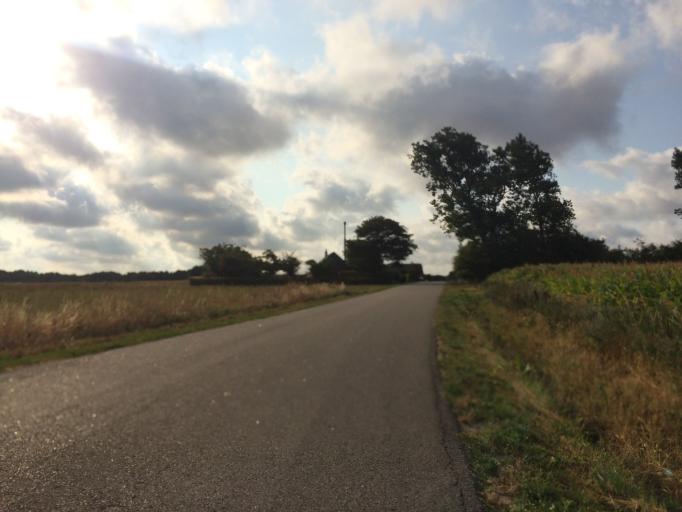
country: DK
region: Central Jutland
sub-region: Holstebro Kommune
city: Vinderup
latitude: 56.6118
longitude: 8.7769
